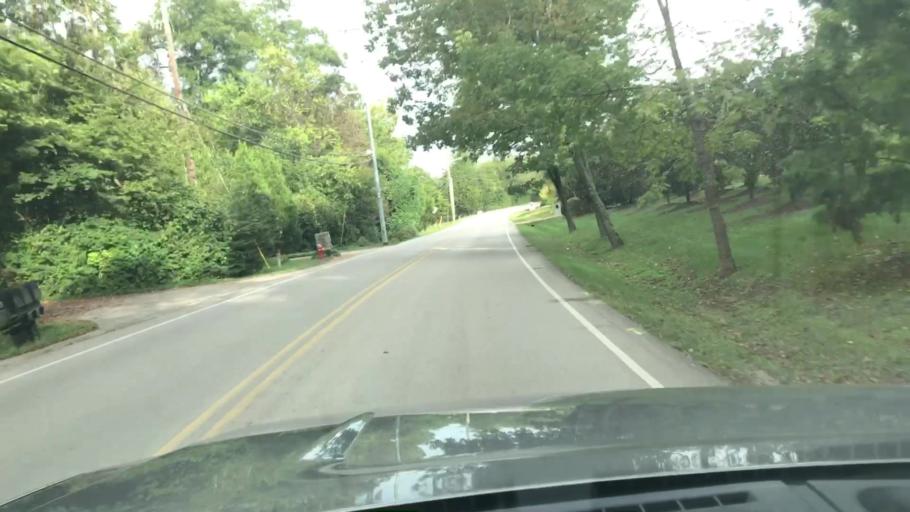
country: US
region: Tennessee
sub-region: Davidson County
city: Forest Hills
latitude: 36.0711
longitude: -86.8302
